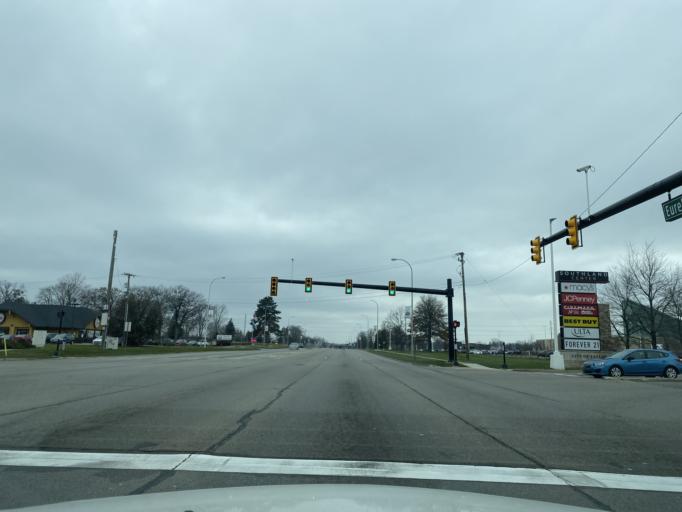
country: US
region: Michigan
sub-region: Wayne County
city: Taylor
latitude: 42.1980
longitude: -83.2512
